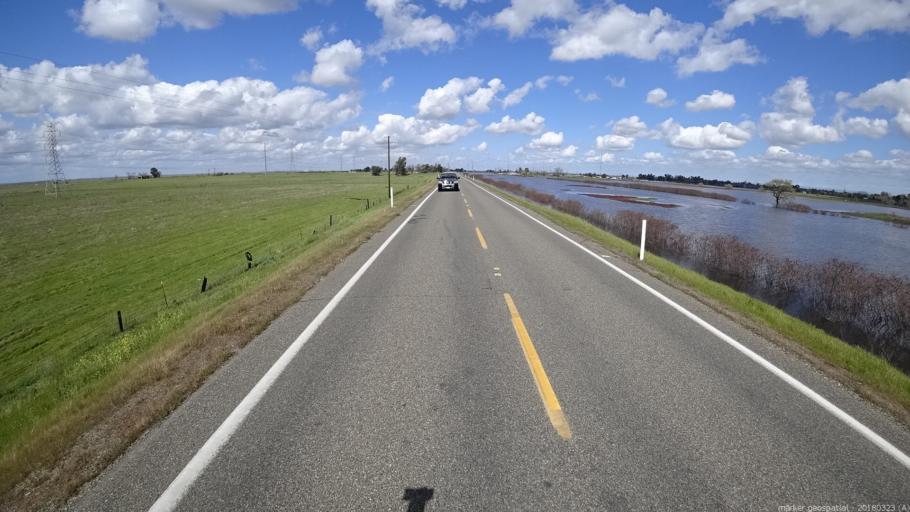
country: US
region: California
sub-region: Sacramento County
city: Elverta
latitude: 38.6909
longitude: -121.4856
